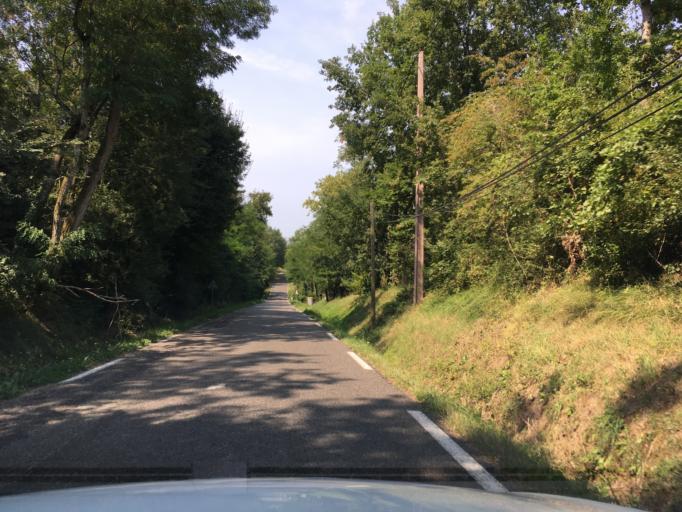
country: FR
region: Midi-Pyrenees
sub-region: Departement du Tarn-et-Garonne
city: Montauban
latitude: 43.9916
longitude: 1.3767
